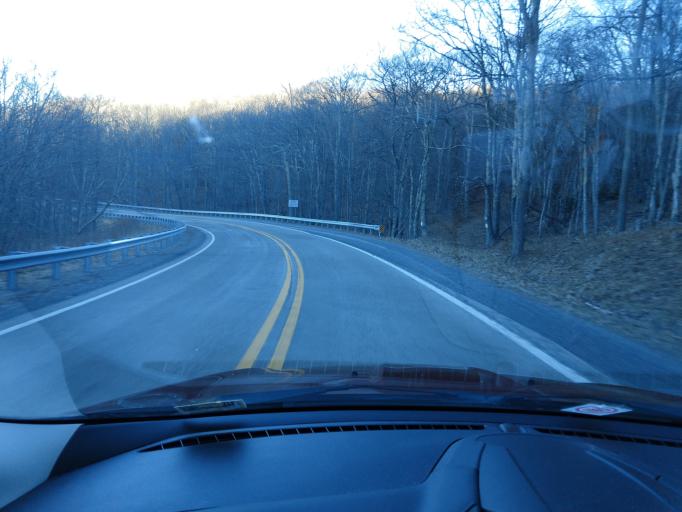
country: US
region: Virginia
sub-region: Highland County
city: Monterey
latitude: 38.4788
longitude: -79.6975
